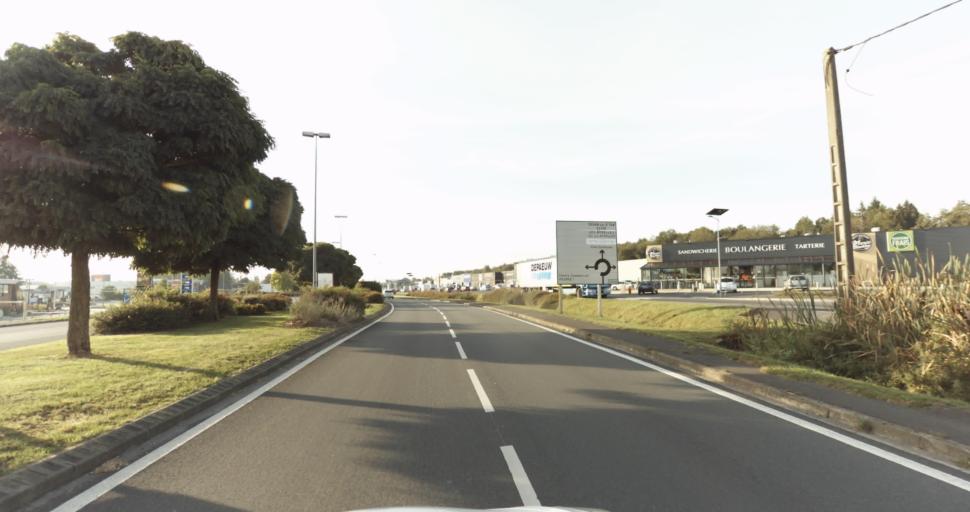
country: FR
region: Champagne-Ardenne
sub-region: Departement des Ardennes
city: Villers-Semeuse
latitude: 49.7337
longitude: 4.7514
